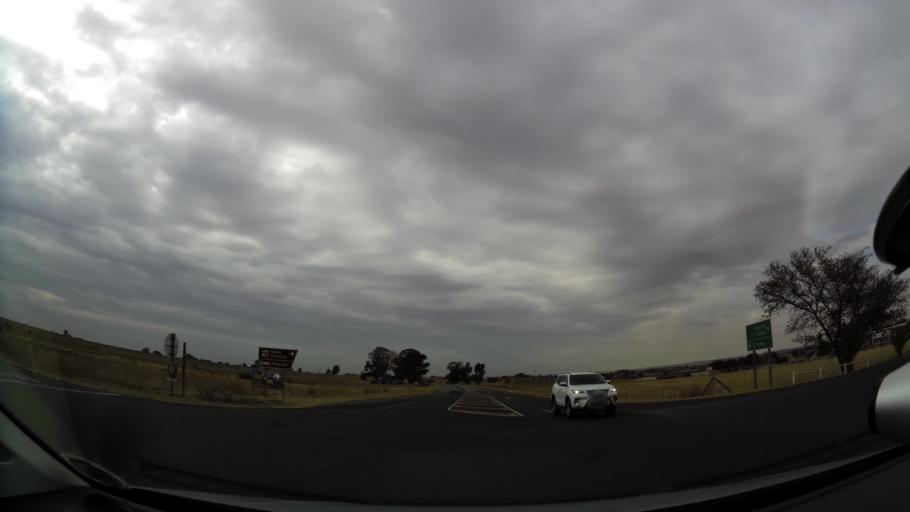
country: ZA
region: Orange Free State
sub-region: Fezile Dabi District Municipality
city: Kroonstad
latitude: -27.6250
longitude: 27.2567
